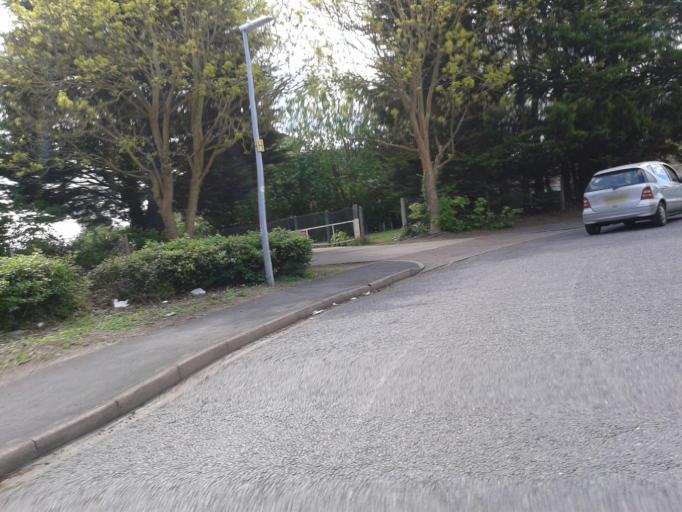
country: GB
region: England
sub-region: Cambridgeshire
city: Cambridge
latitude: 52.2269
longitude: 0.1528
